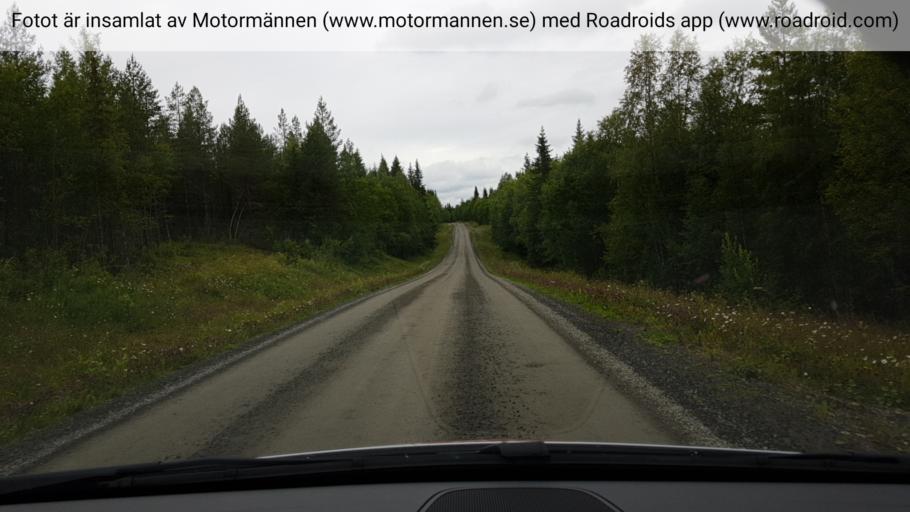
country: SE
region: Jaemtland
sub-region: Krokoms Kommun
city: Krokom
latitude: 63.7483
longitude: 14.4625
